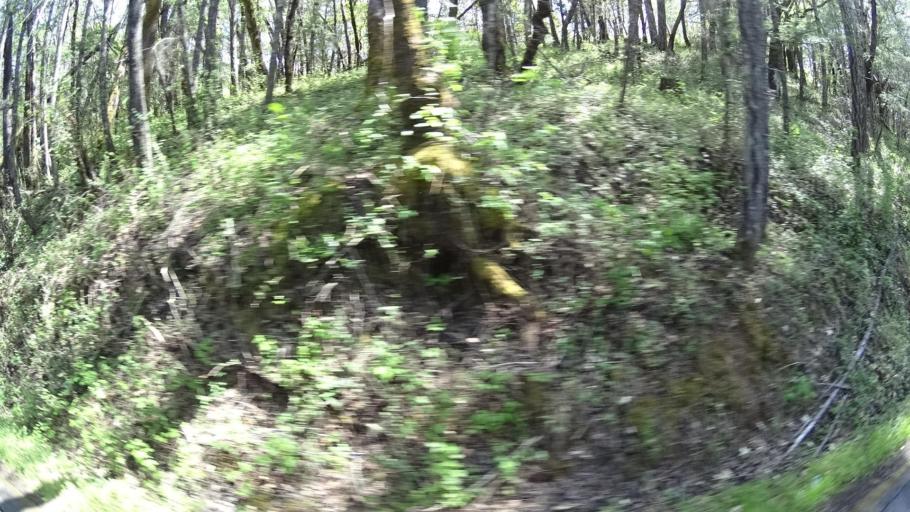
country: US
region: California
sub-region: Humboldt County
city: Redway
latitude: 40.2473
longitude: -123.6241
